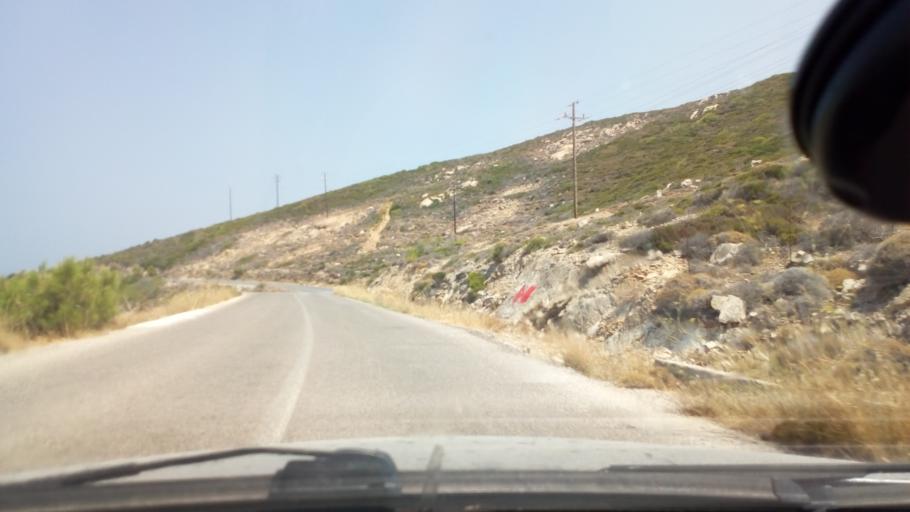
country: GR
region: North Aegean
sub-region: Nomos Samou
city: Agios Kirykos
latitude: 37.6327
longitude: 26.1160
